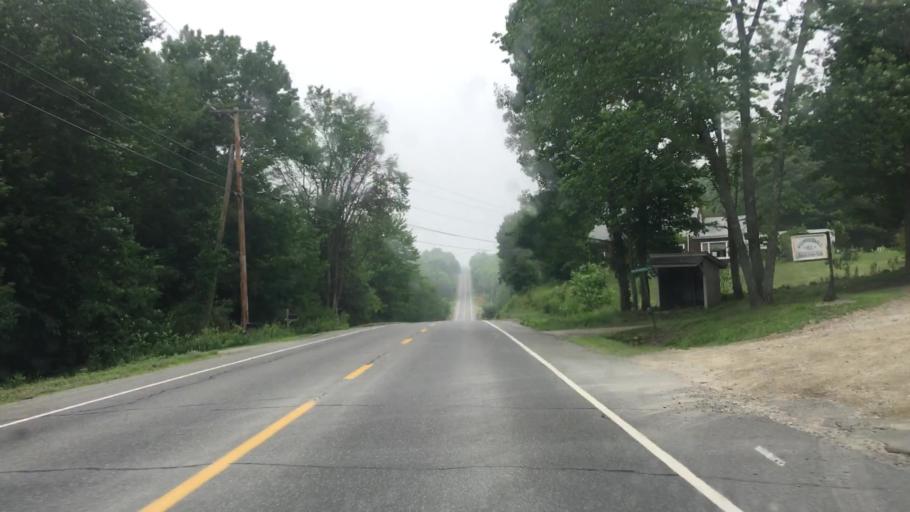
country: US
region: Maine
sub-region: Lincoln County
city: Wiscasset
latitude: 44.0722
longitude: -69.6955
